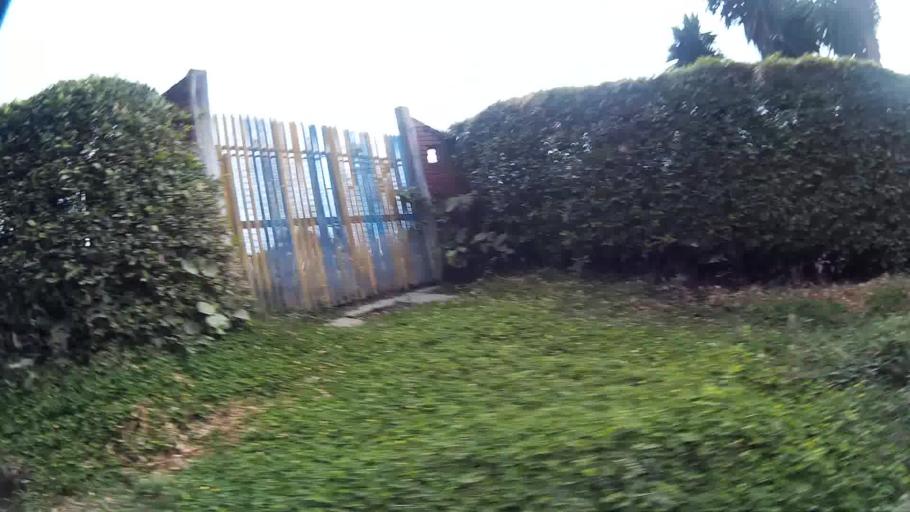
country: CO
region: Valle del Cauca
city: Ulloa
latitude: 4.7351
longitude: -75.7364
